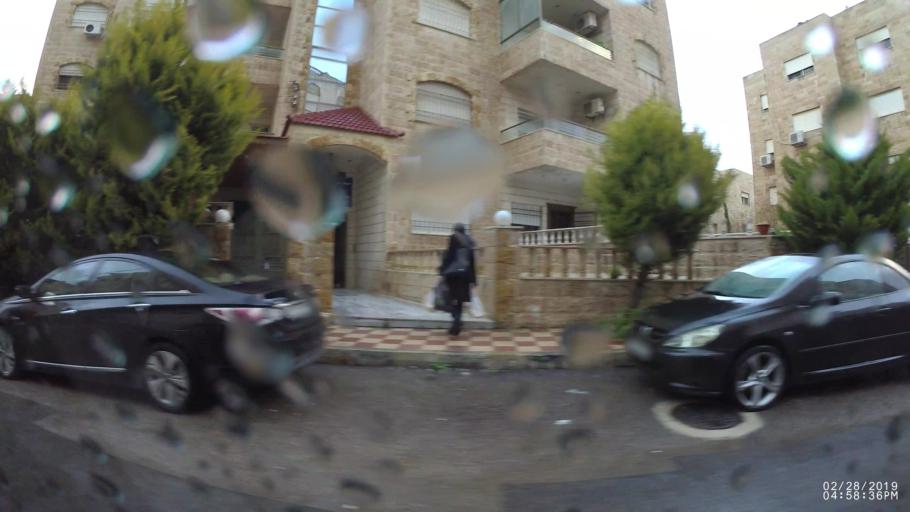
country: JO
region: Amman
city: Amman
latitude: 31.9991
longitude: 35.9302
